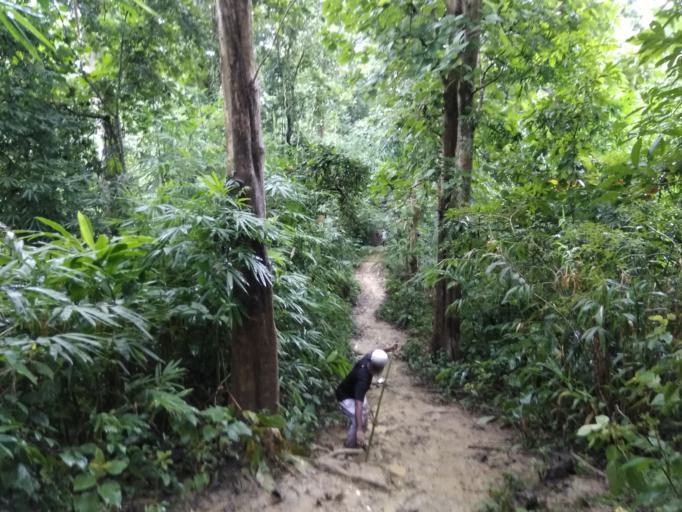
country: IN
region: Tripura
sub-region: Dhalai
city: Kamalpur
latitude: 24.1703
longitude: 91.8963
